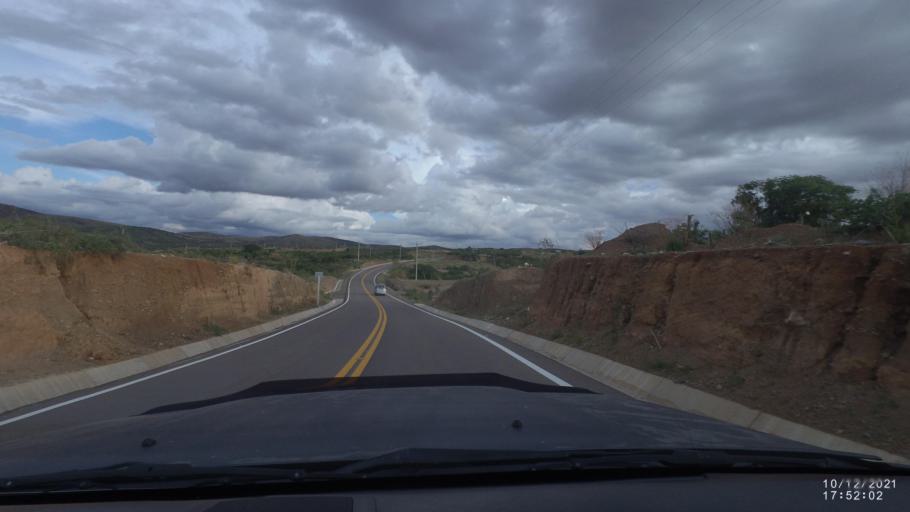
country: BO
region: Cochabamba
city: Cliza
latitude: -17.6820
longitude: -65.9544
